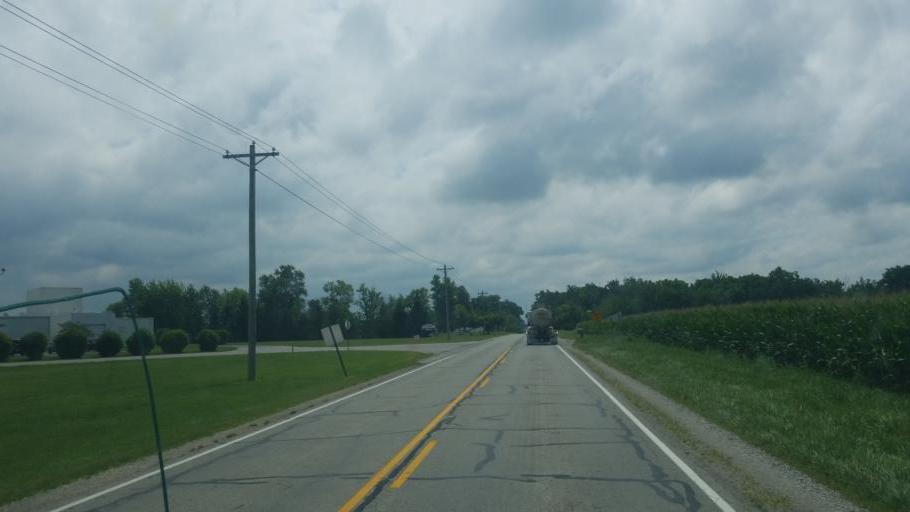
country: US
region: Indiana
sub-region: Huntington County
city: Warren
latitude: 40.6722
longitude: -85.4152
